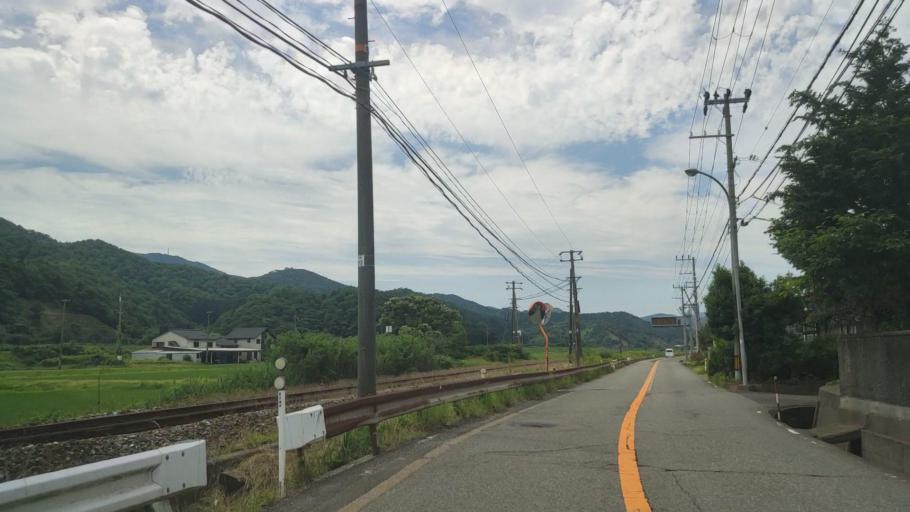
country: JP
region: Hyogo
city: Toyooka
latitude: 35.6422
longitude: 134.7582
